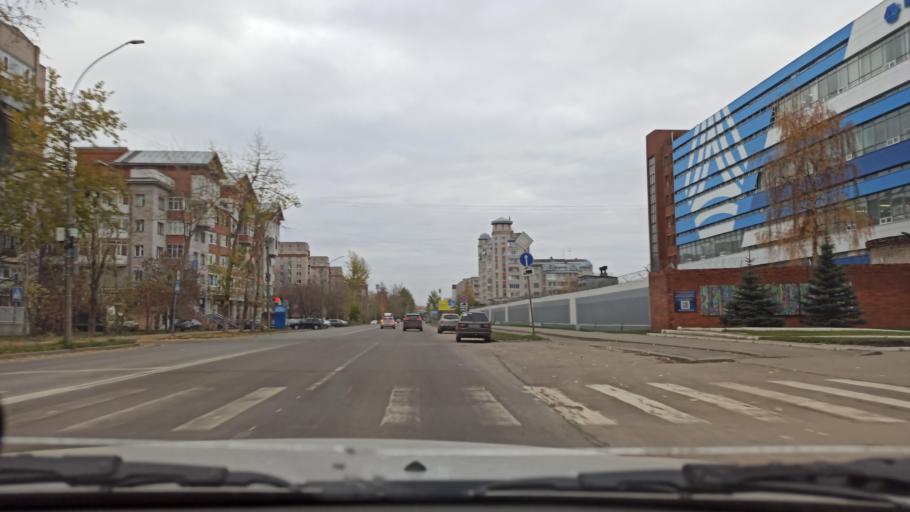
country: RU
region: Vologda
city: Vologda
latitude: 59.2164
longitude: 39.8709
